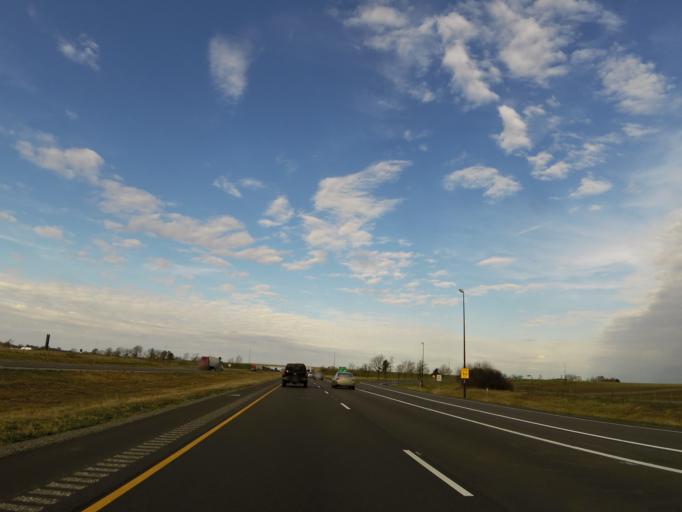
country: US
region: Illinois
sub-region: Washington County
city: Okawville
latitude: 38.4372
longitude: -89.5250
